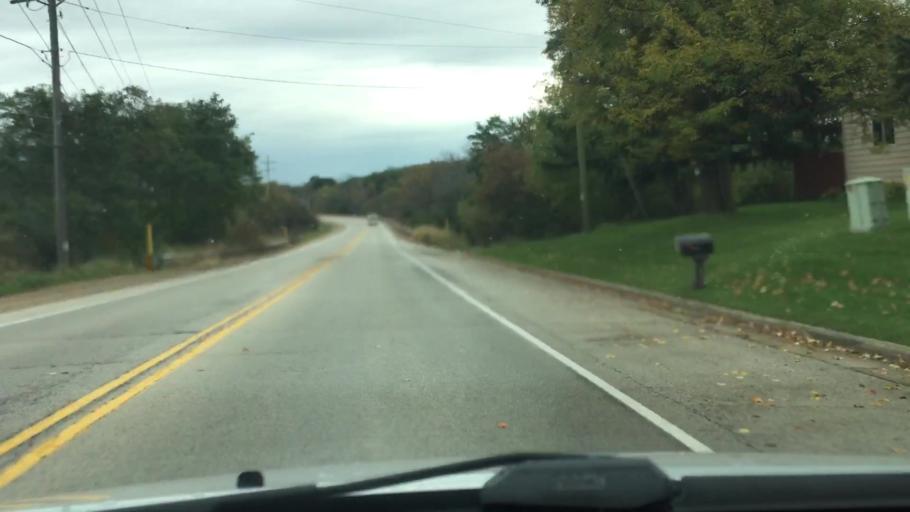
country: US
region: Wisconsin
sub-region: Waukesha County
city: Wales
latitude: 43.0200
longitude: -88.3228
